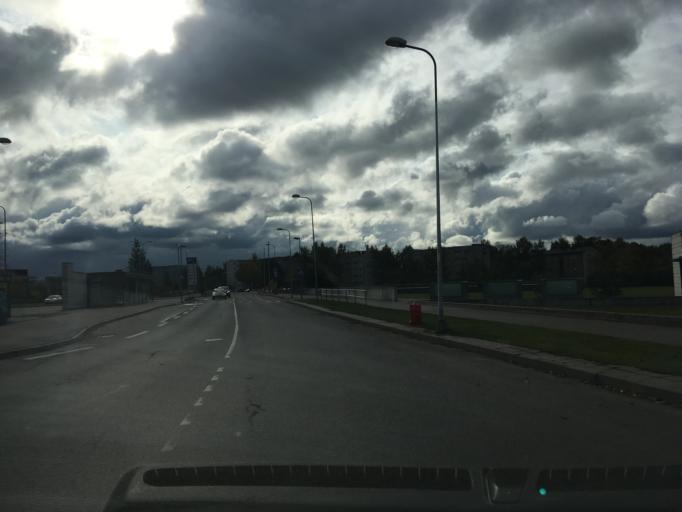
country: EE
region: Harju
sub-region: Tallinna linn
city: Tallinn
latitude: 59.4364
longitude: 24.7987
